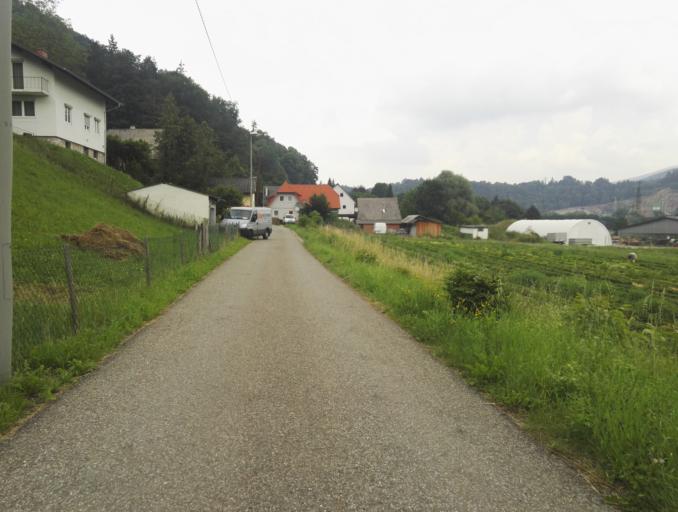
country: AT
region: Styria
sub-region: Politischer Bezirk Graz-Umgebung
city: Gratkorn
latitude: 47.1132
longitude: 15.3700
